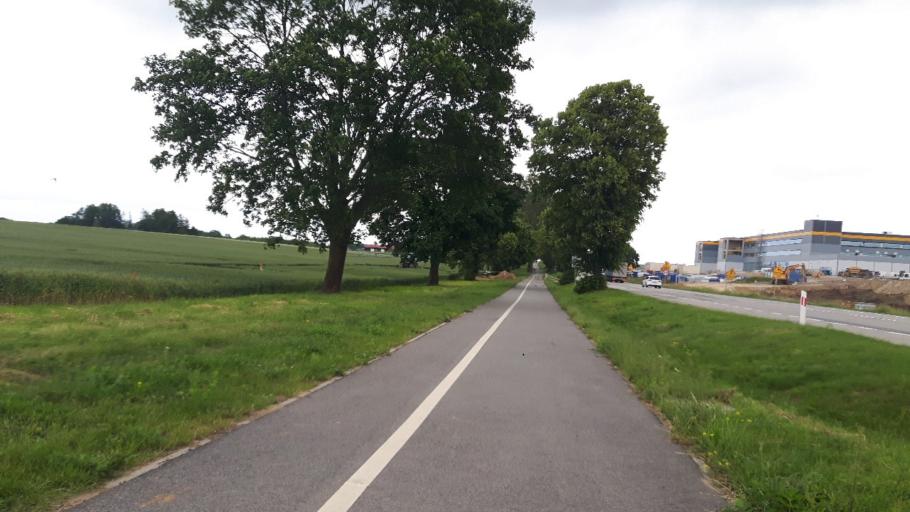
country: PL
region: West Pomeranian Voivodeship
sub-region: Powiat policki
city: Kolbaskowo
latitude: 53.3438
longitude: 14.4484
